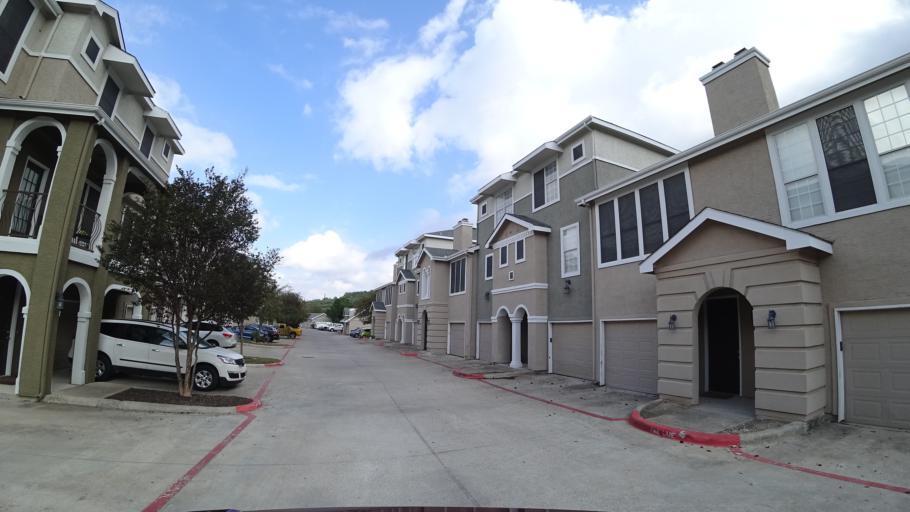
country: US
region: Texas
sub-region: Travis County
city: Hudson Bend
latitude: 30.3833
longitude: -97.8768
